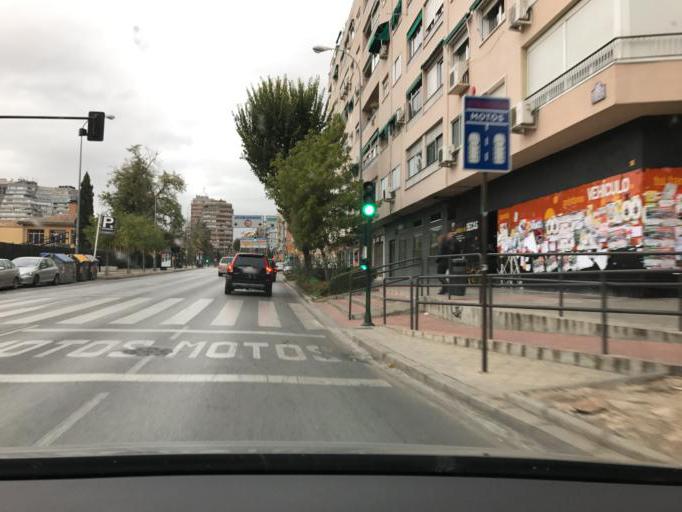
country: ES
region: Andalusia
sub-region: Provincia de Granada
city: Granada
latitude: 37.1816
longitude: -3.6060
